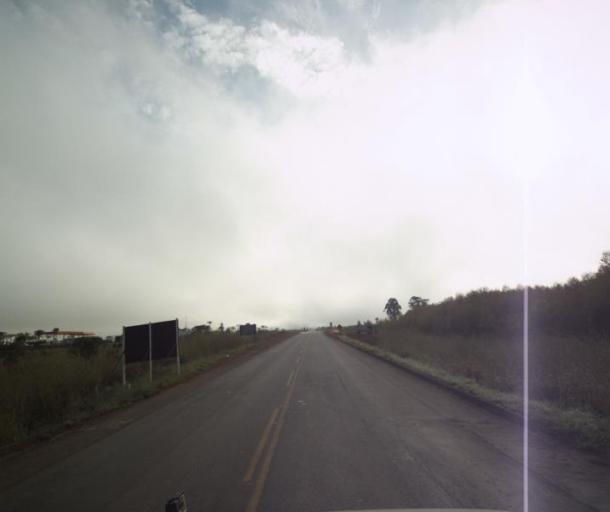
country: BR
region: Goias
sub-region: Pirenopolis
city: Pirenopolis
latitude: -15.7568
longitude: -48.7526
